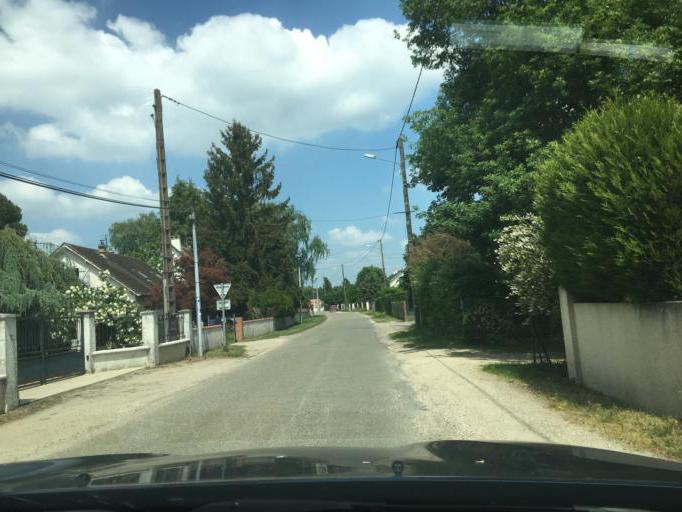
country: FR
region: Centre
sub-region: Departement du Loiret
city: Trainou
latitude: 47.9876
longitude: 2.1111
